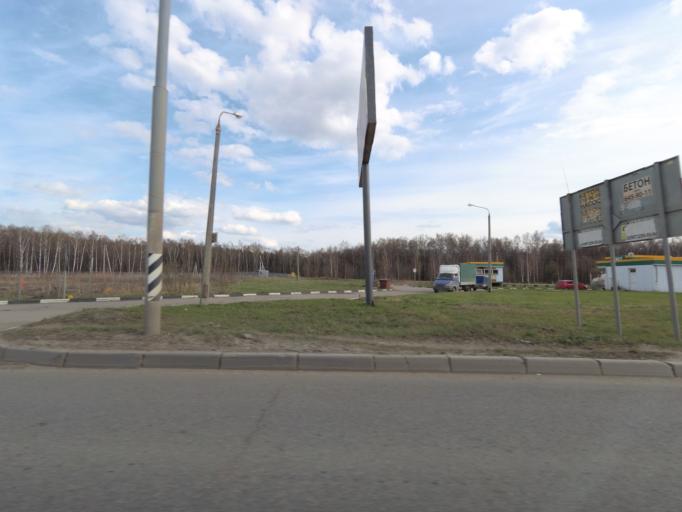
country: RU
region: Moskovskaya
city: Lobnya
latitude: 56.0006
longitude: 37.4249
